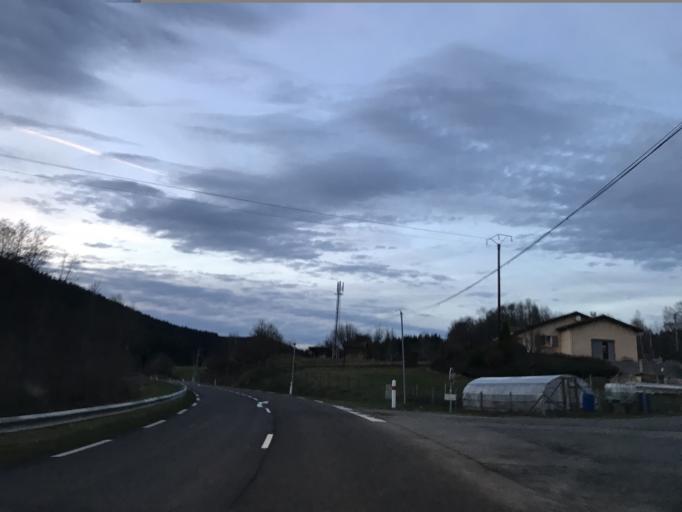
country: FR
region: Rhone-Alpes
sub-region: Departement de la Loire
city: Noiretable
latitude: 45.8415
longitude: 3.7460
